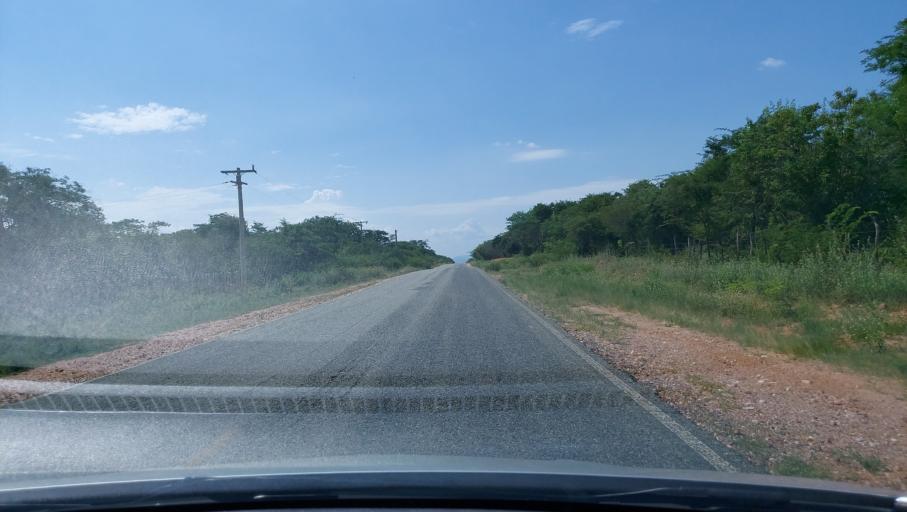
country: BR
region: Bahia
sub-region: Oliveira Dos Brejinhos
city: Beira Rio
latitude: -12.1774
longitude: -42.5432
